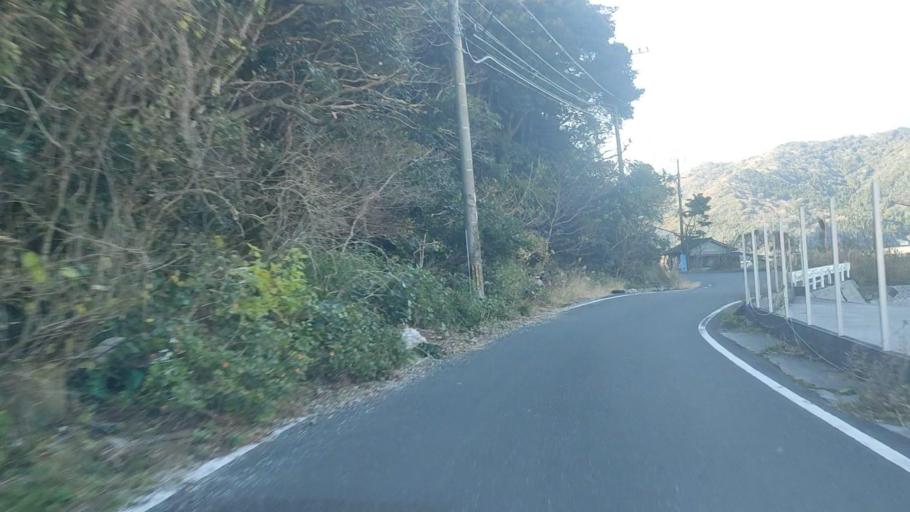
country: JP
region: Oita
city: Saiki
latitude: 32.7968
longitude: 131.8978
